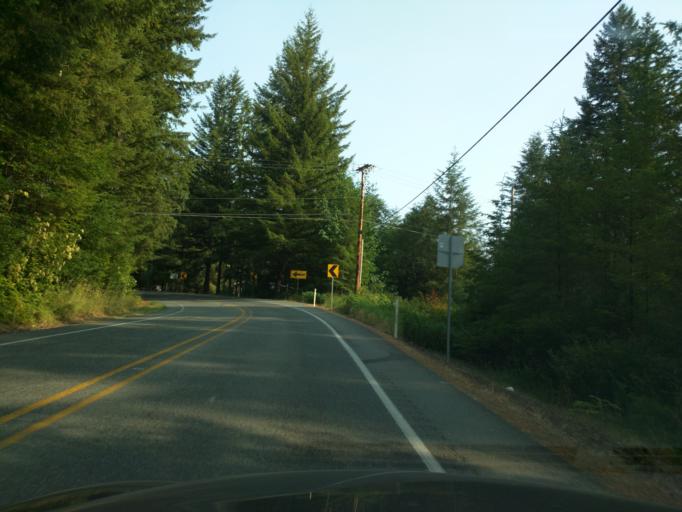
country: US
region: Washington
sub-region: Whatcom County
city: Peaceful Valley
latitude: 48.9361
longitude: -122.1463
